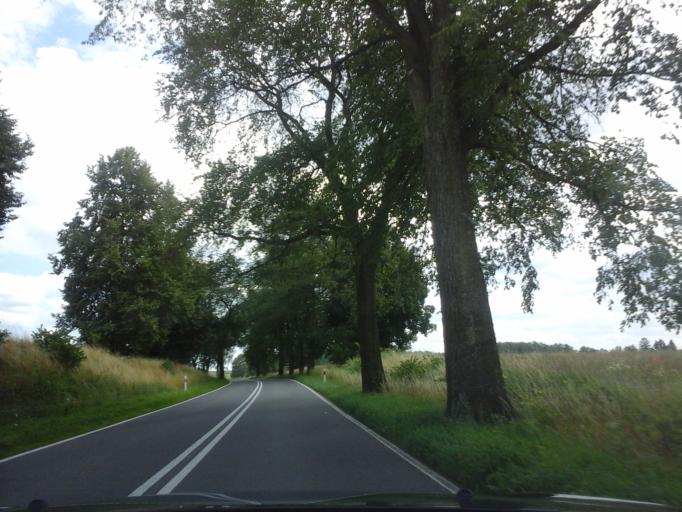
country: PL
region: West Pomeranian Voivodeship
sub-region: Powiat choszczenski
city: Recz
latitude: 53.2872
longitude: 15.5521
